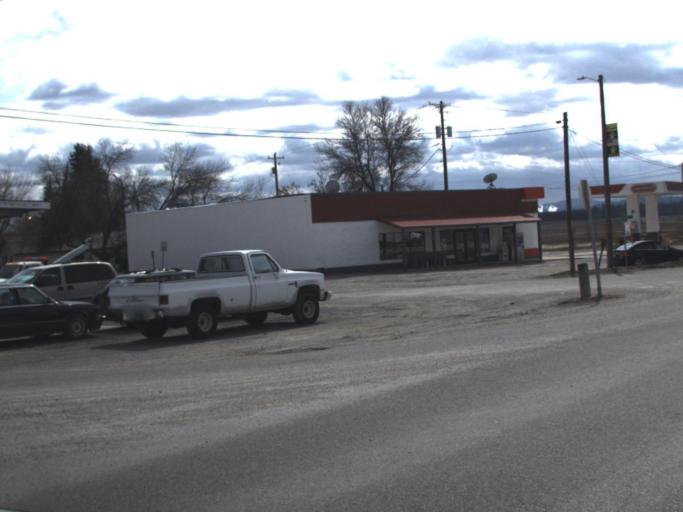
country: US
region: Washington
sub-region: Pend Oreille County
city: Newport
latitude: 48.3376
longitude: -117.3044
